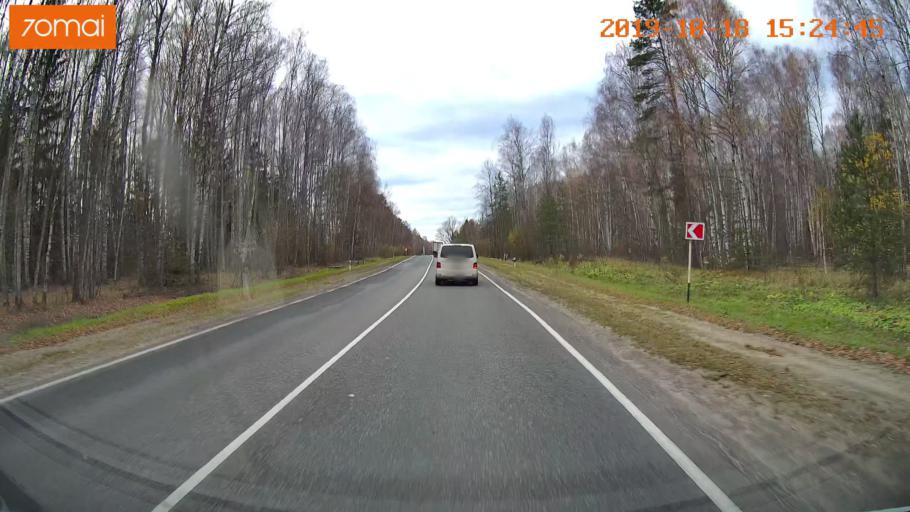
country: RU
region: Vladimir
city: Anopino
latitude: 55.7370
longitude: 40.7182
